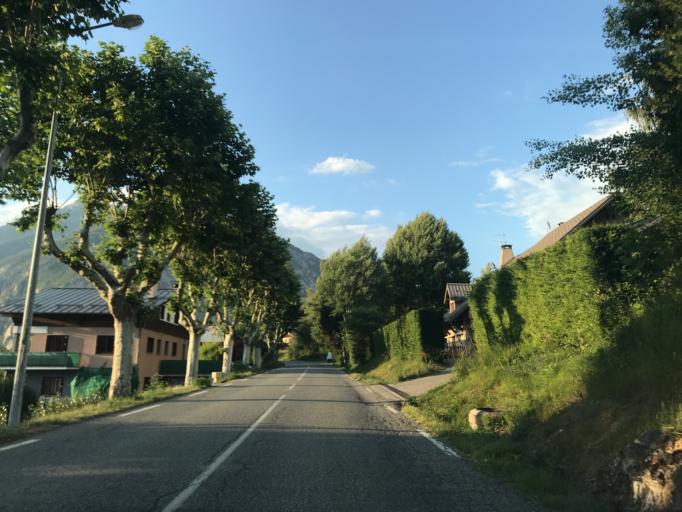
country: FR
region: Provence-Alpes-Cote d'Azur
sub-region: Departement des Hautes-Alpes
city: Guillestre
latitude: 44.6567
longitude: 6.6559
